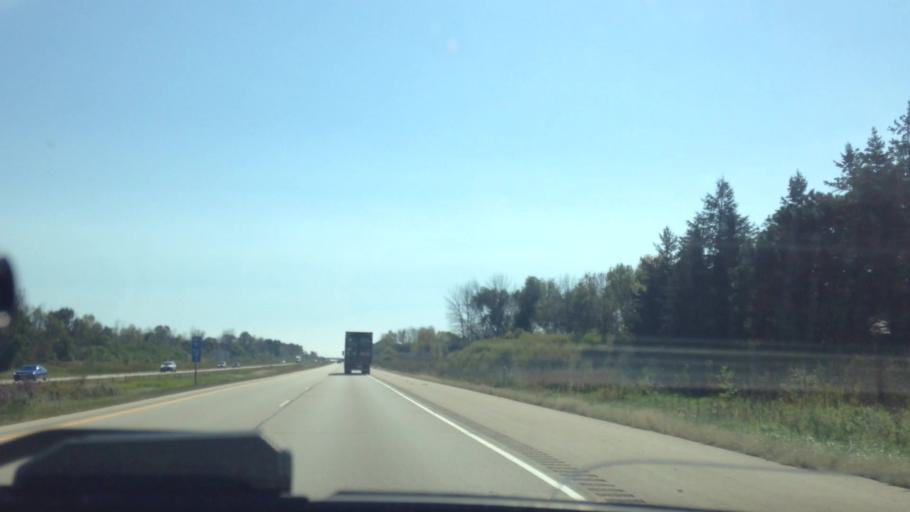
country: US
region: Wisconsin
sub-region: Ozaukee County
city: Grafton
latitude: 43.2649
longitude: -87.9201
